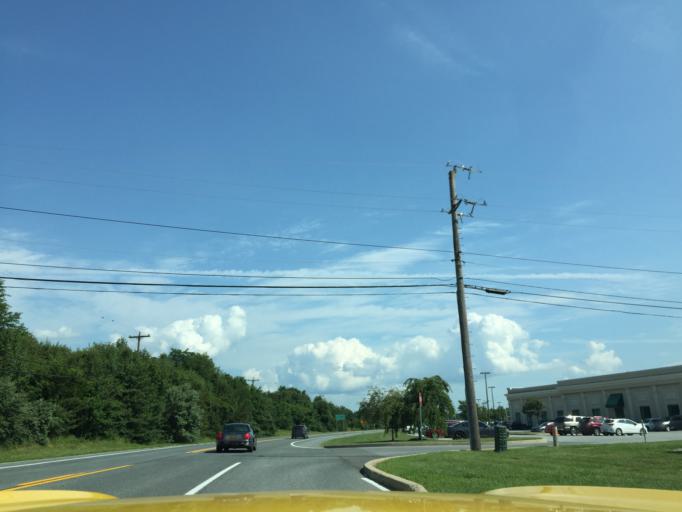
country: US
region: Delaware
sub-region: New Castle County
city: Wilmington Manor
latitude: 39.6687
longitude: -75.6128
